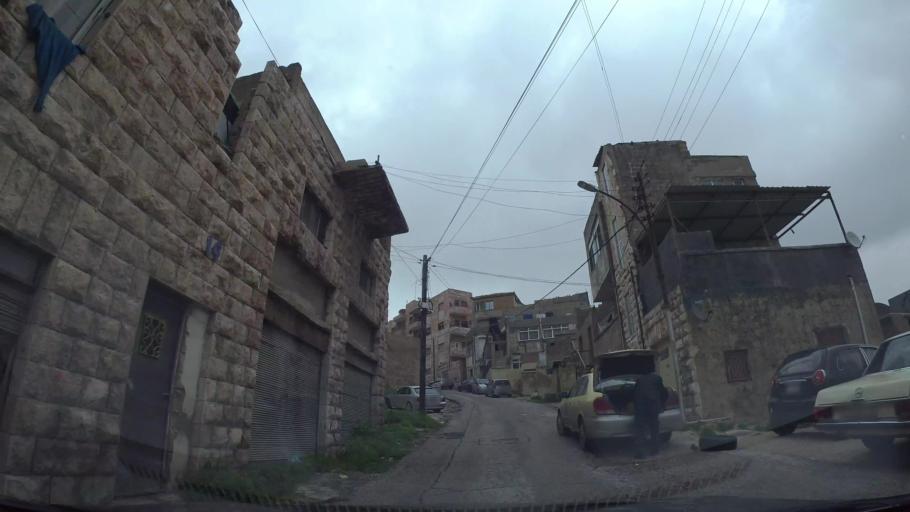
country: JO
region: Amman
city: Amman
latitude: 31.9474
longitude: 35.9223
